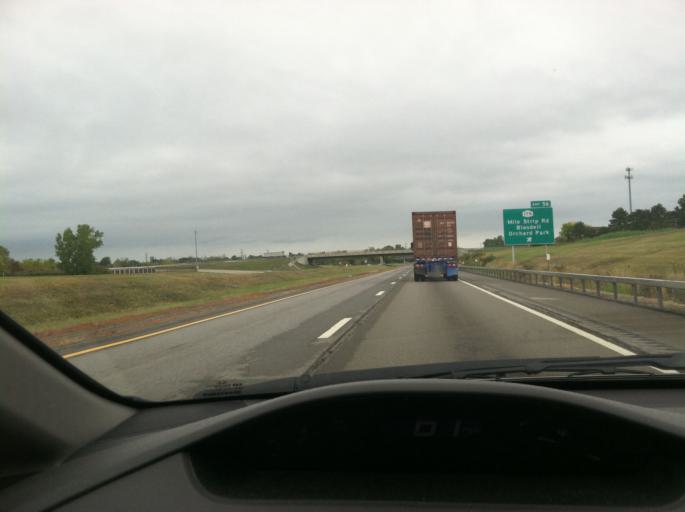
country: US
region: New York
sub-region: Erie County
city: Blasdell
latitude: 42.7869
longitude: -78.8159
